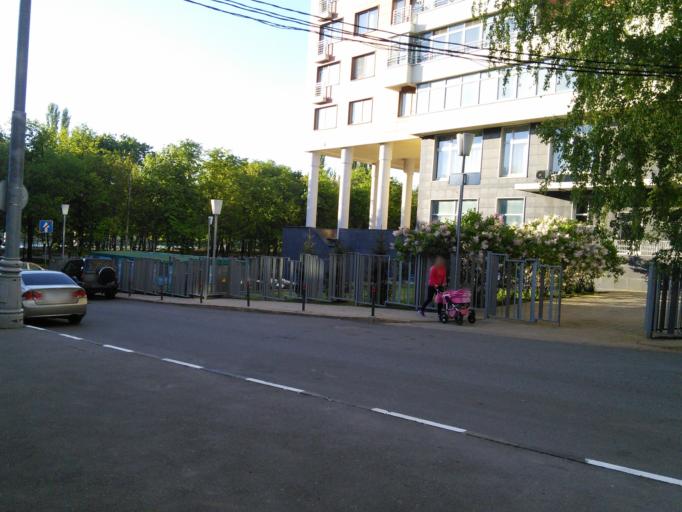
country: RU
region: Moskovskaya
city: Leninskiye Gory
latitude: 55.7019
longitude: 37.5616
